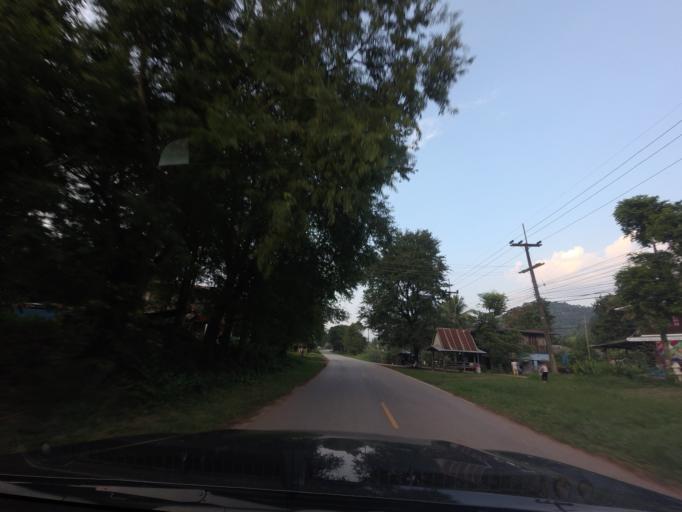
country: TH
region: Loei
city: Na Haeo
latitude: 17.4465
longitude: 101.0561
